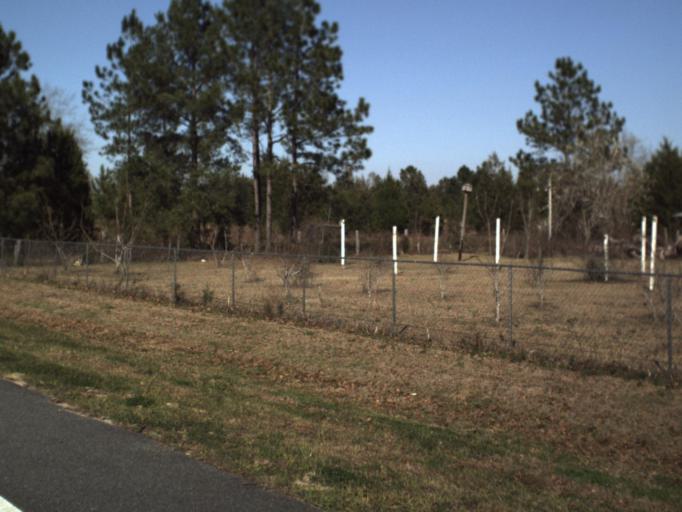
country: US
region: Florida
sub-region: Gulf County
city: Wewahitchka
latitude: 30.2857
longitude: -85.2417
